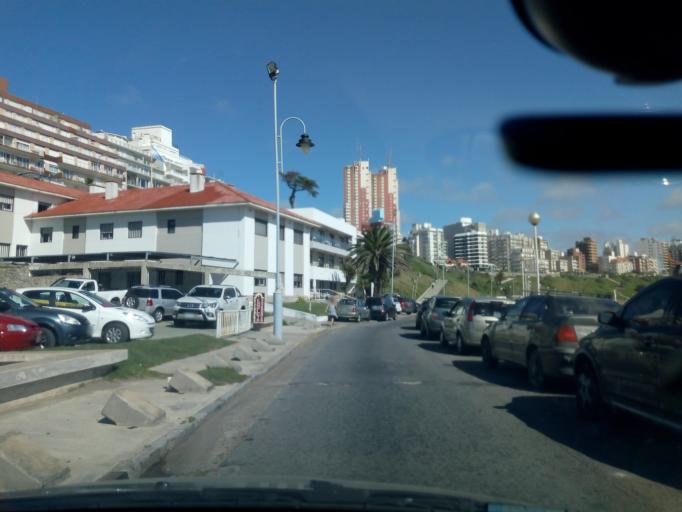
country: AR
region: Buenos Aires
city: Mar del Plata
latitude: -38.0164
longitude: -57.5255
